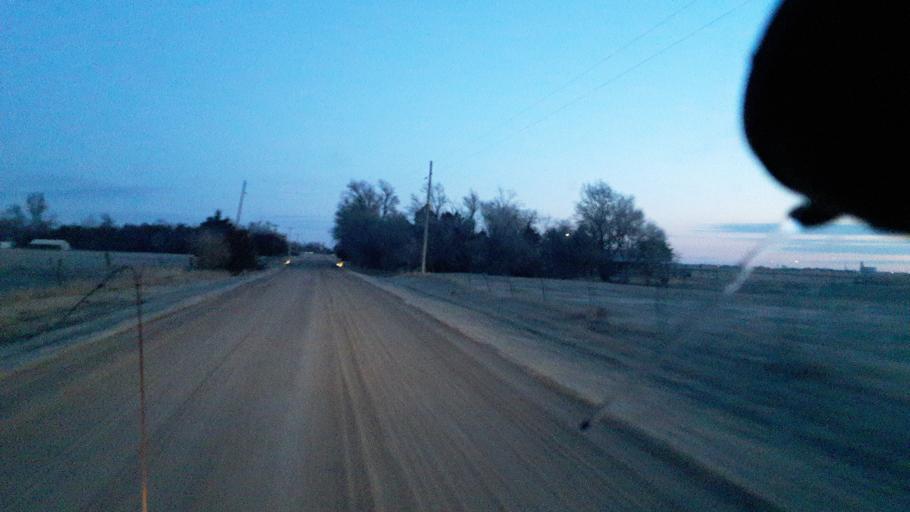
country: US
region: Kansas
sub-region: Reno County
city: South Hutchinson
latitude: 37.9945
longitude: -97.9767
